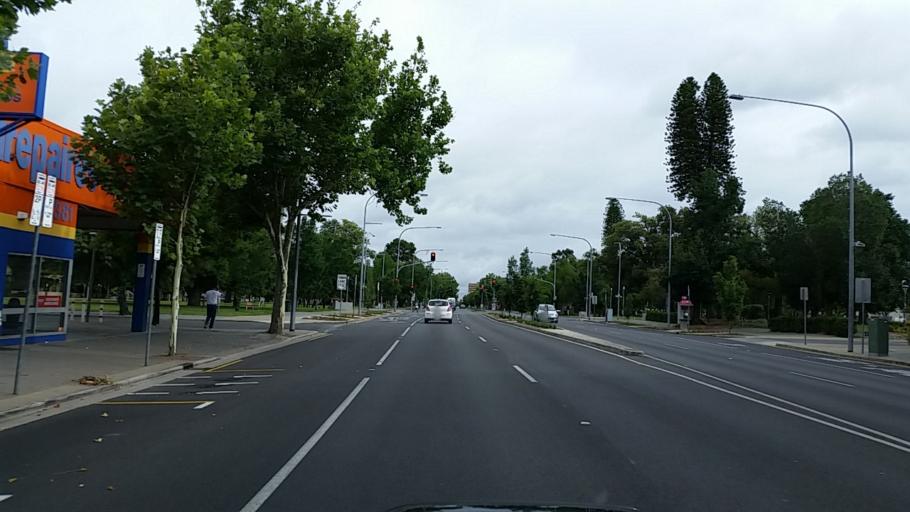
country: AU
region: South Australia
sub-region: Adelaide
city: Adelaide
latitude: -34.9337
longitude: 138.6064
